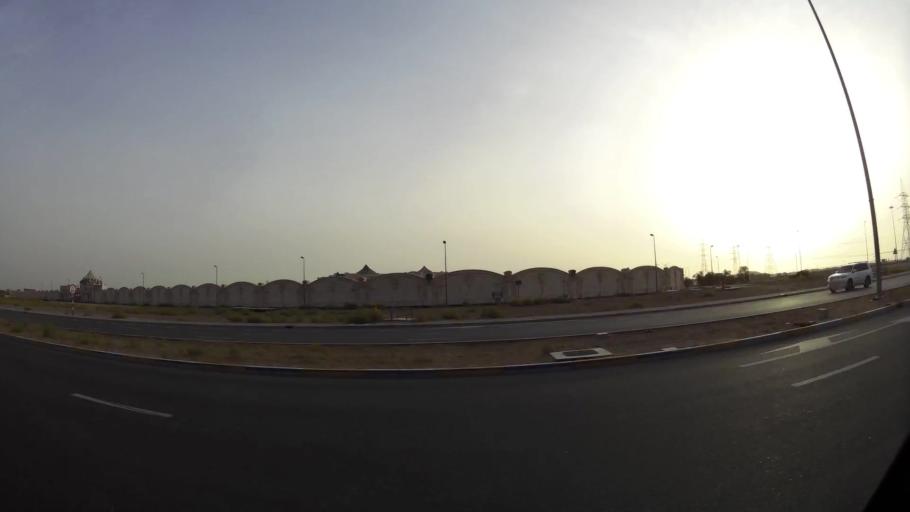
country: OM
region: Al Buraimi
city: Al Buraymi
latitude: 24.2733
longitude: 55.7203
